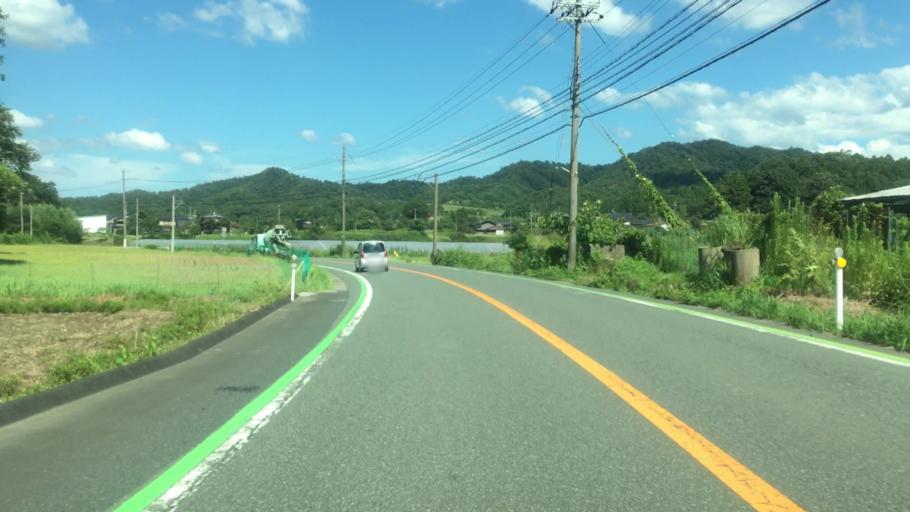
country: JP
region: Kyoto
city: Miyazu
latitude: 35.5816
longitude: 135.0338
